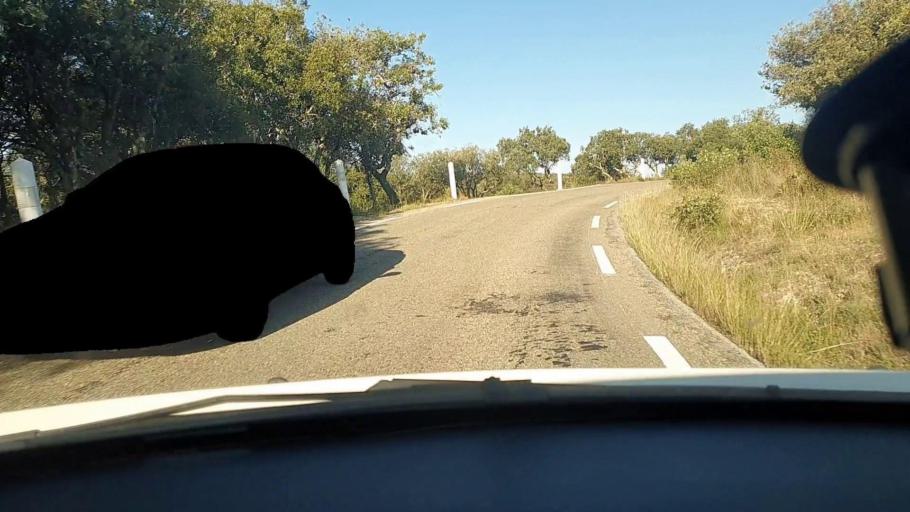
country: FR
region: Languedoc-Roussillon
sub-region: Departement du Gard
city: Goudargues
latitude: 44.1548
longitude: 4.3562
